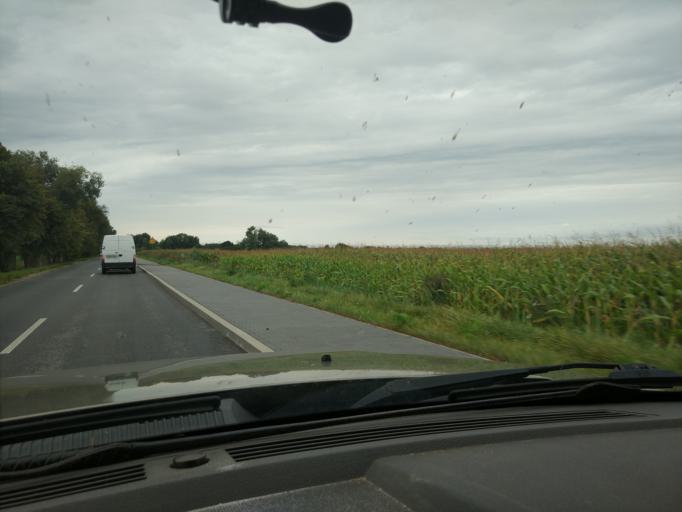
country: PL
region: Masovian Voivodeship
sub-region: Powiat pruszkowski
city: Brwinow
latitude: 52.1605
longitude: 20.7345
